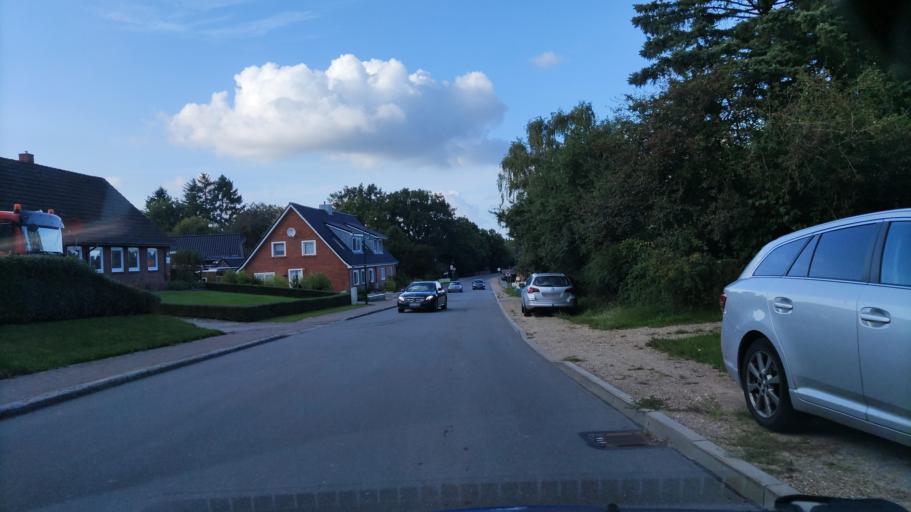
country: DE
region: Schleswig-Holstein
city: Glasau
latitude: 54.0514
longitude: 10.5301
